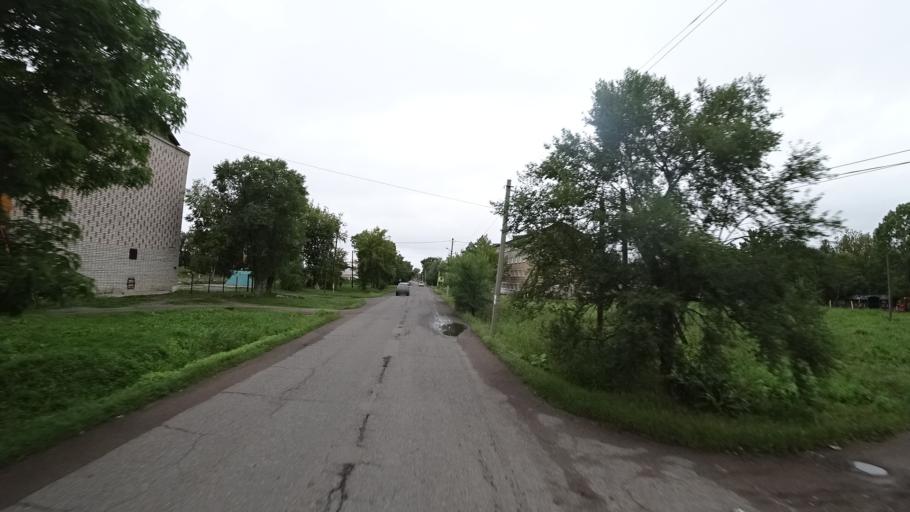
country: RU
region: Primorskiy
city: Chernigovka
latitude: 44.3387
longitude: 132.5784
